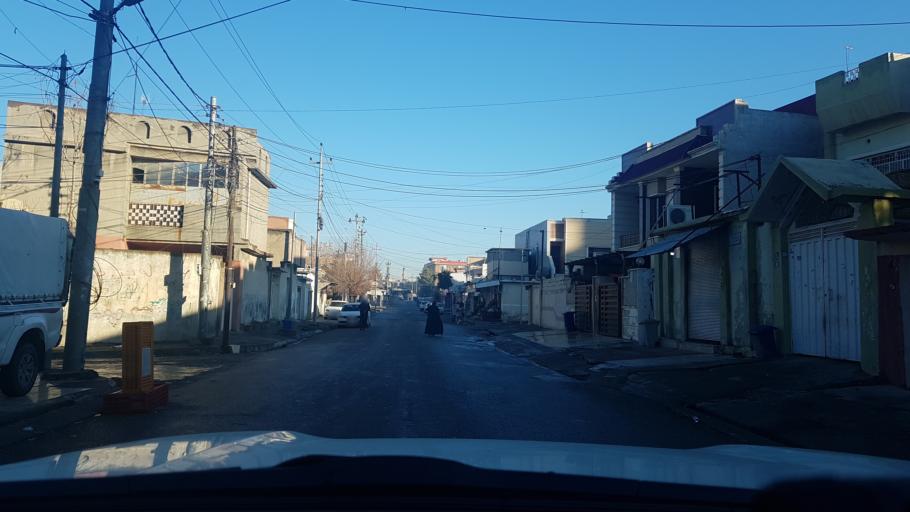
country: IQ
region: Arbil
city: Erbil
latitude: 36.2044
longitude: 44.0084
